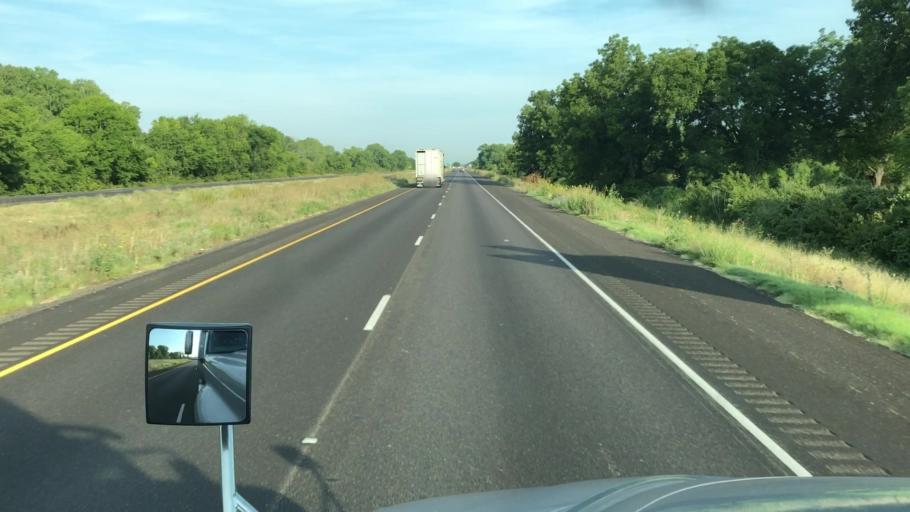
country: US
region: Texas
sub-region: McLennan County
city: Bellmead
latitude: 31.5416
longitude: -97.0499
